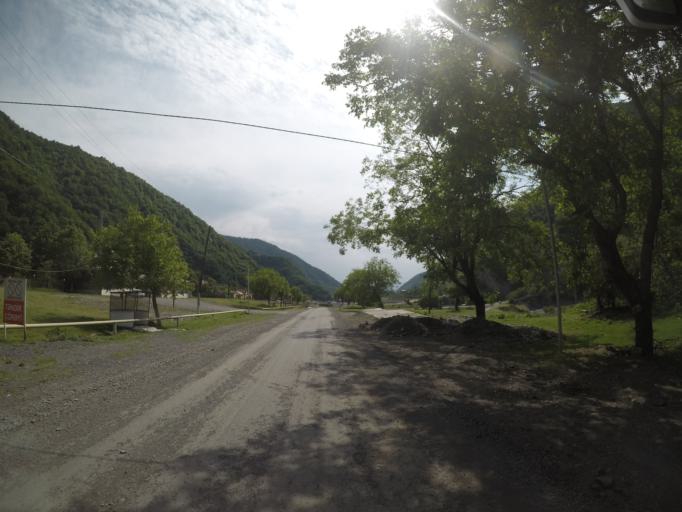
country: AZ
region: Qakh Rayon
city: Qaxbas
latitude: 41.4587
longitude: 47.0261
